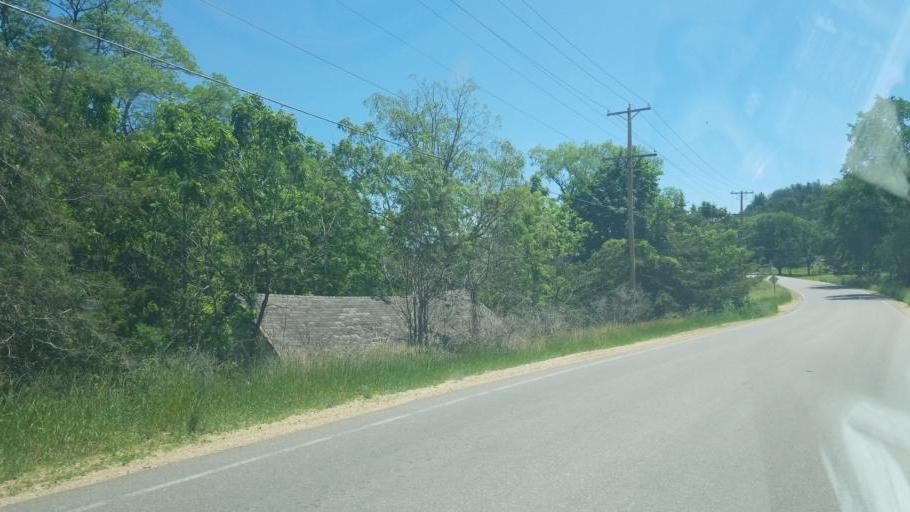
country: US
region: Wisconsin
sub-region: Juneau County
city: New Lisbon
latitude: 43.9184
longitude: -90.2670
